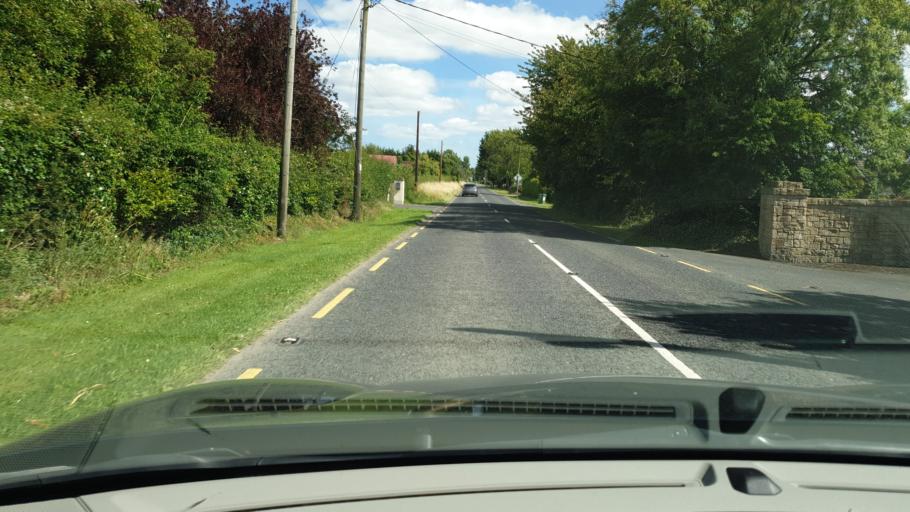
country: IE
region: Leinster
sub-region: An Mhi
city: Dunboyne
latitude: 53.4306
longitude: -6.5086
